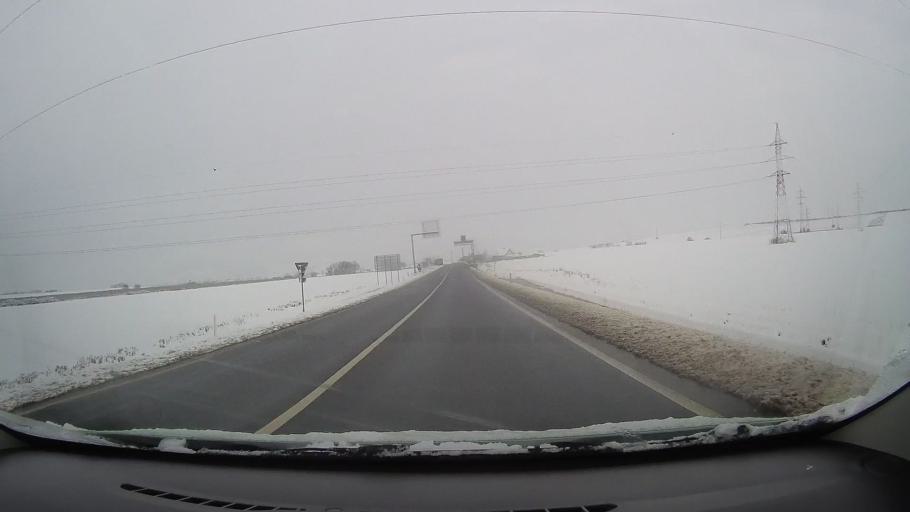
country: RO
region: Alba
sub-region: Municipiul Sebes
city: Lancram
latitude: 45.9801
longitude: 23.5192
